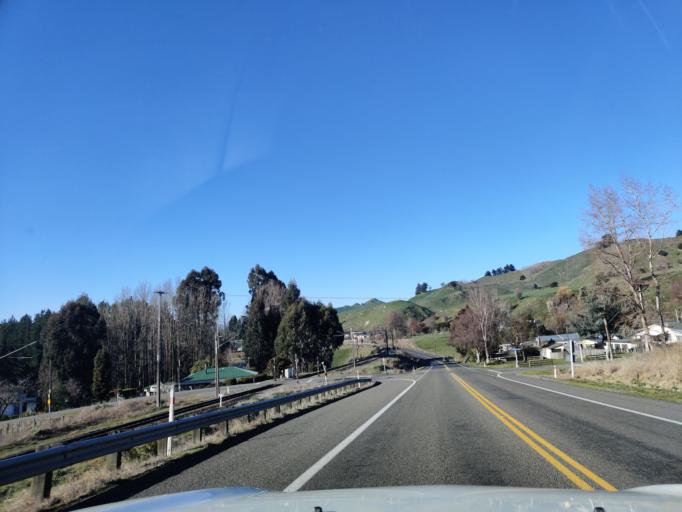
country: NZ
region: Manawatu-Wanganui
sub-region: Ruapehu District
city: Waiouru
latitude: -39.6864
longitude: 175.8073
